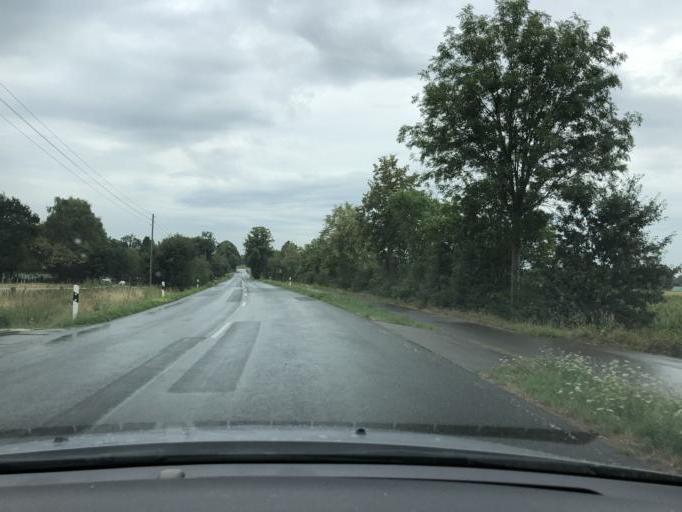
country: DE
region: North Rhine-Westphalia
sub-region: Regierungsbezirk Dusseldorf
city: Schermbeck
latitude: 51.7209
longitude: 6.8694
